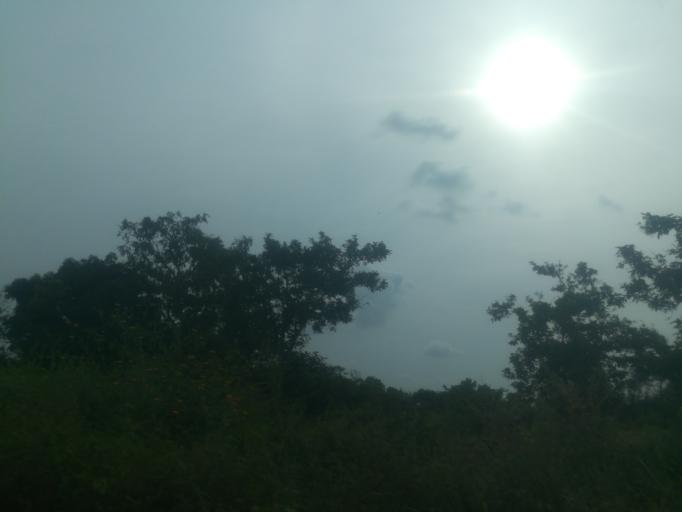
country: NG
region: Ogun
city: Ayetoro
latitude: 7.2873
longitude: 3.0846
